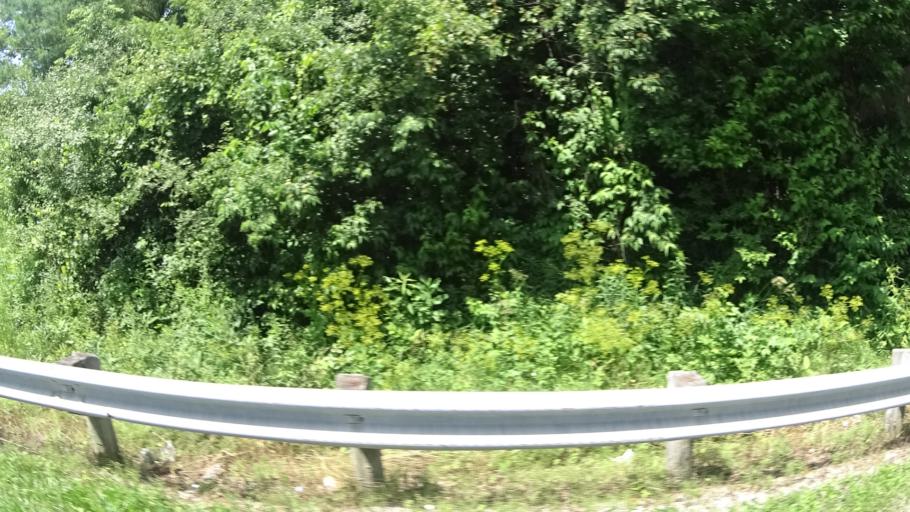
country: US
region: Ohio
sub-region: Erie County
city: Huron
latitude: 41.3487
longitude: -82.5123
